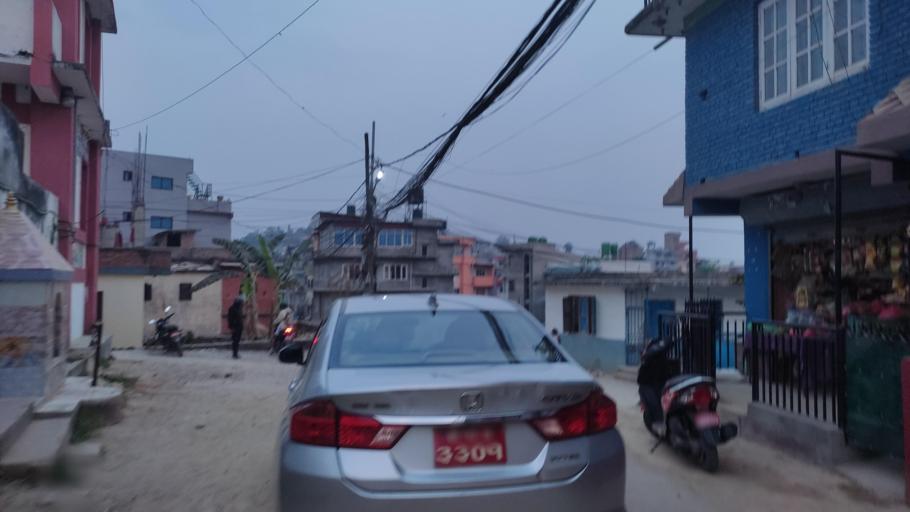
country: NP
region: Central Region
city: Kirtipur
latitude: 27.6725
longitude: 85.2837
